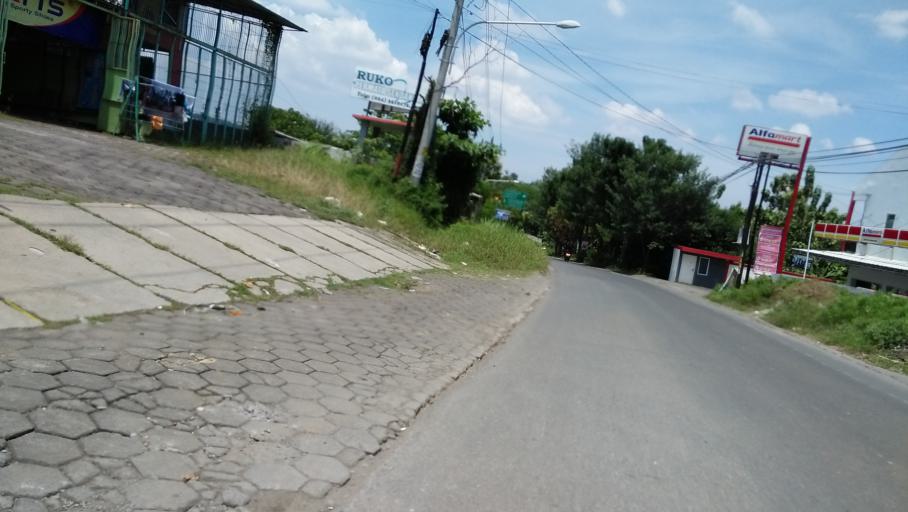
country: ID
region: Central Java
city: Mranggen
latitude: -7.0441
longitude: 110.4676
